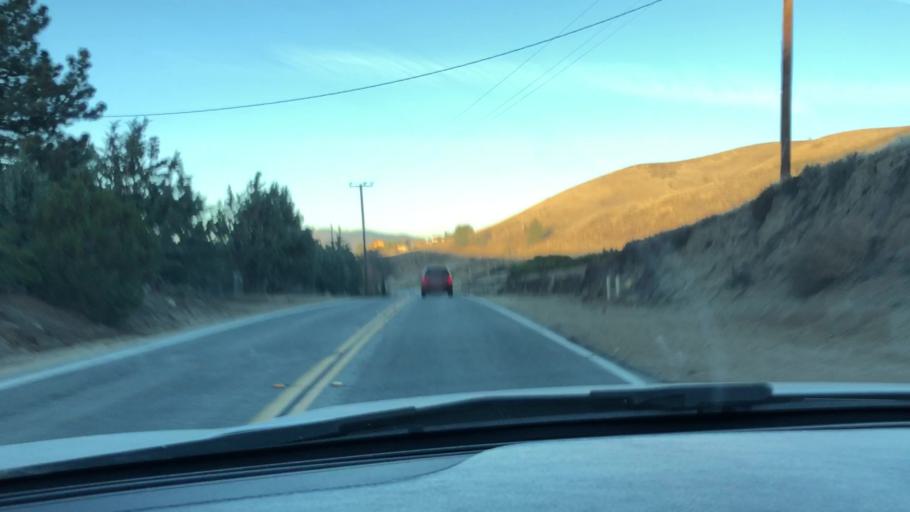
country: US
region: California
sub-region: Los Angeles County
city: Green Valley
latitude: 34.6590
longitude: -118.3554
